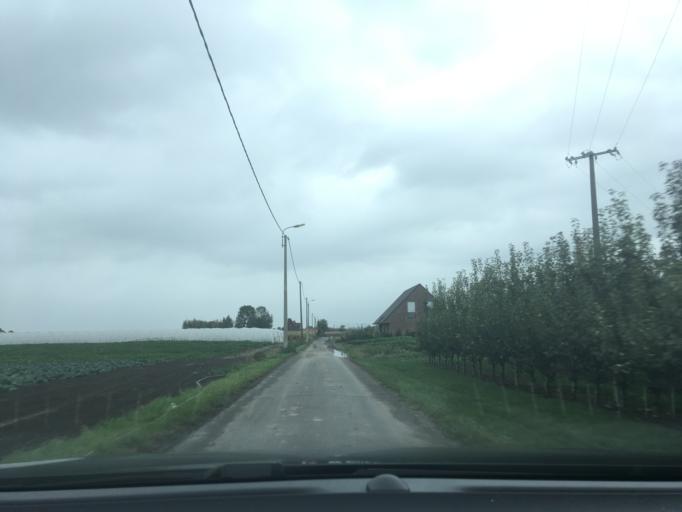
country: BE
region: Flanders
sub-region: Provincie West-Vlaanderen
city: Ledegem
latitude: 50.8806
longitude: 3.1314
